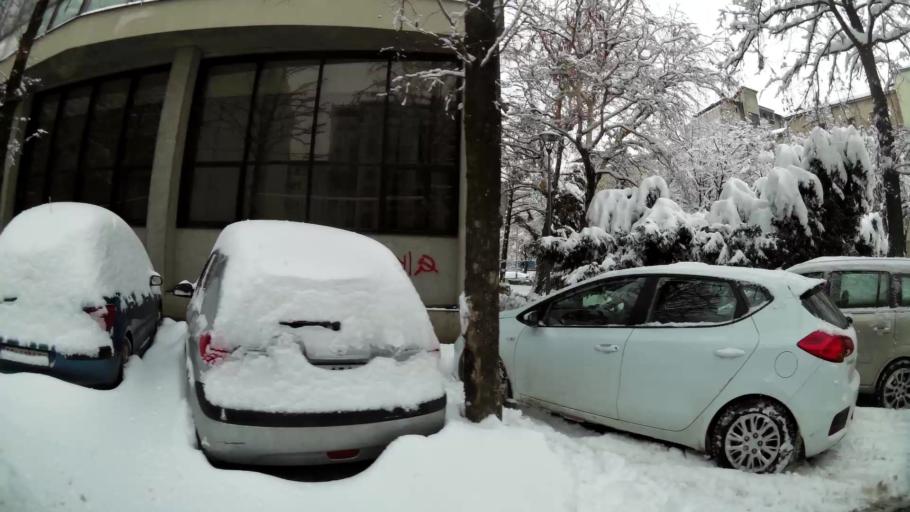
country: RS
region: Central Serbia
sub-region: Belgrade
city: Vracar
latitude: 44.8008
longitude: 20.4742
